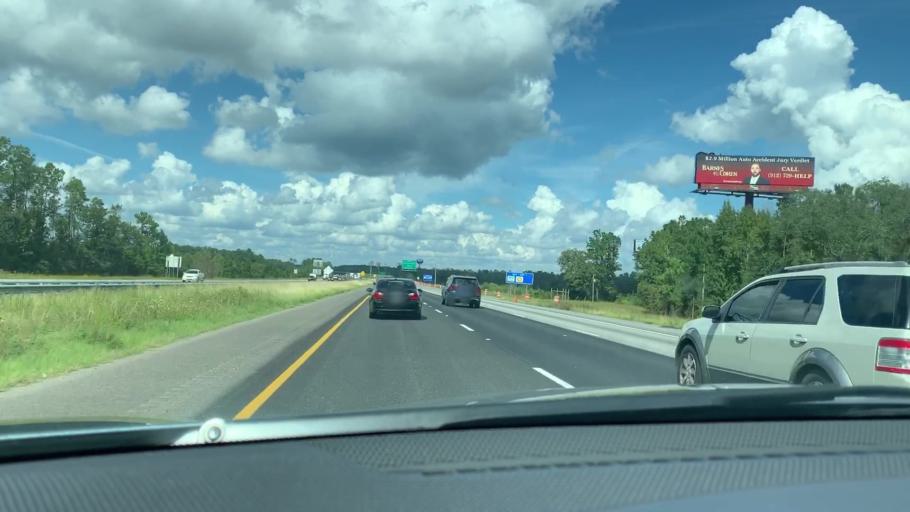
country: US
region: Georgia
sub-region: Camden County
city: Kingsland
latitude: 30.8339
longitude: -81.6683
